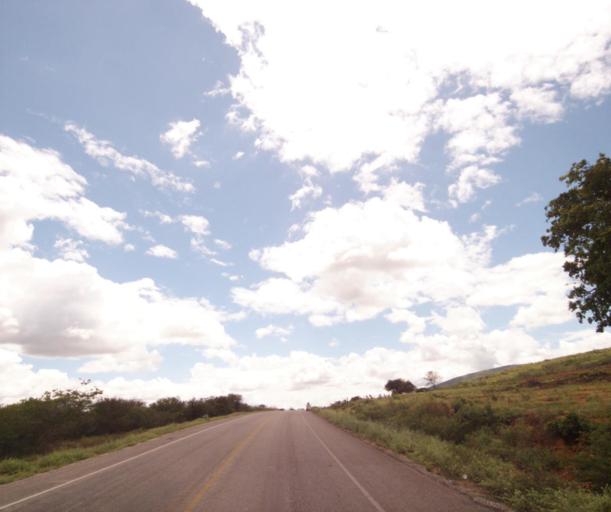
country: BR
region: Bahia
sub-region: Brumado
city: Brumado
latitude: -14.2362
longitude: -41.6906
